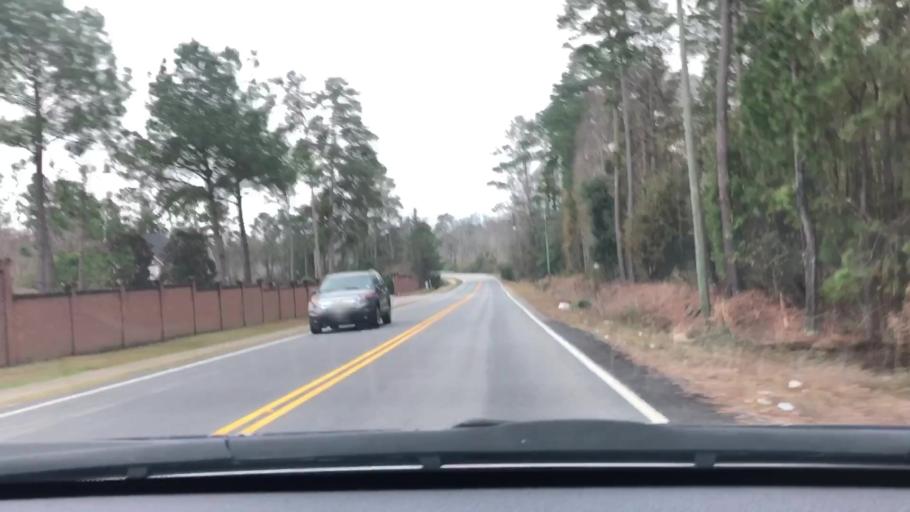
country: US
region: South Carolina
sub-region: Sumter County
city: Cherryvale
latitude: 33.9499
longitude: -80.4024
